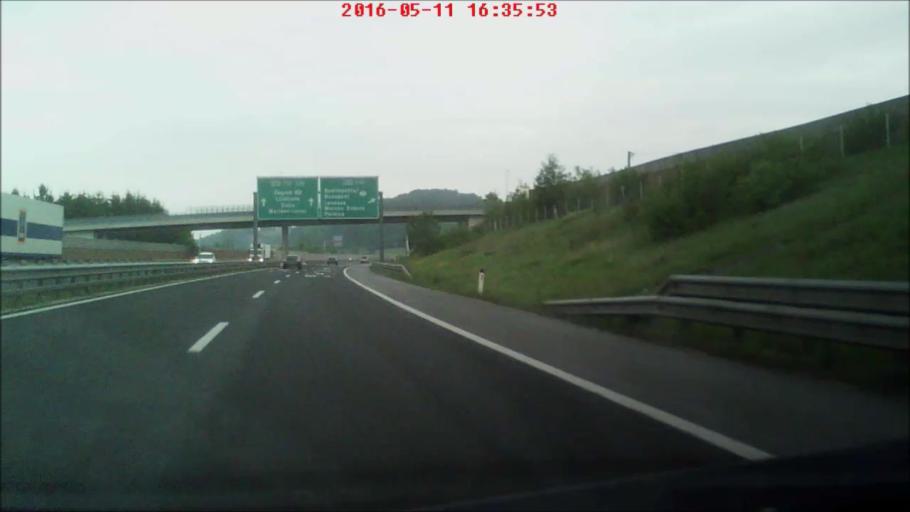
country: SI
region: Pesnica
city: Pesnica pri Mariboru
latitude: 46.5936
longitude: 15.6775
